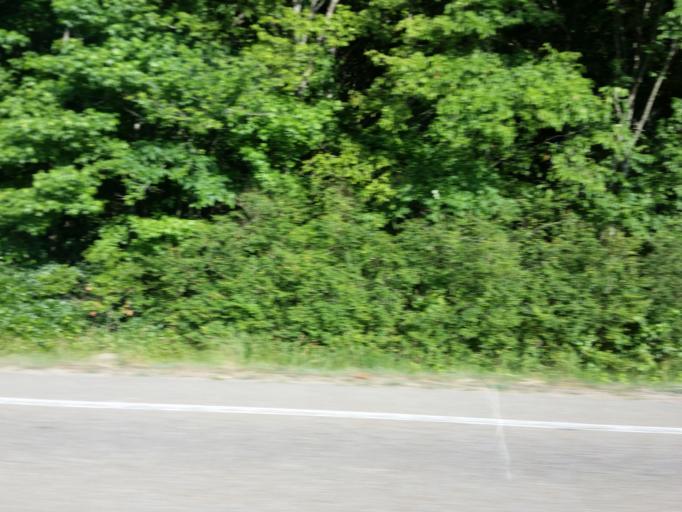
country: US
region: Mississippi
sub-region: Calhoun County
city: Calhoun City
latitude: 33.8207
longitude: -89.3416
